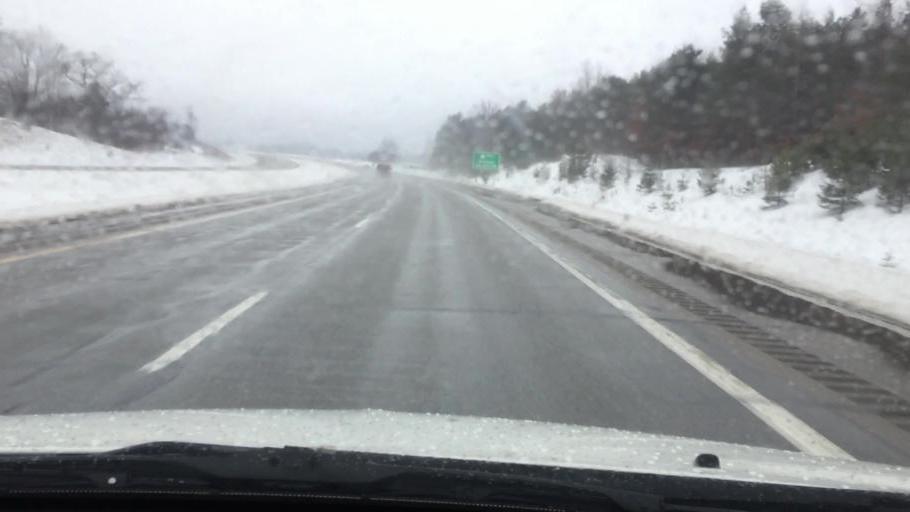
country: US
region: Michigan
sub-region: Wexford County
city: Cadillac
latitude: 44.2665
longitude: -85.3878
